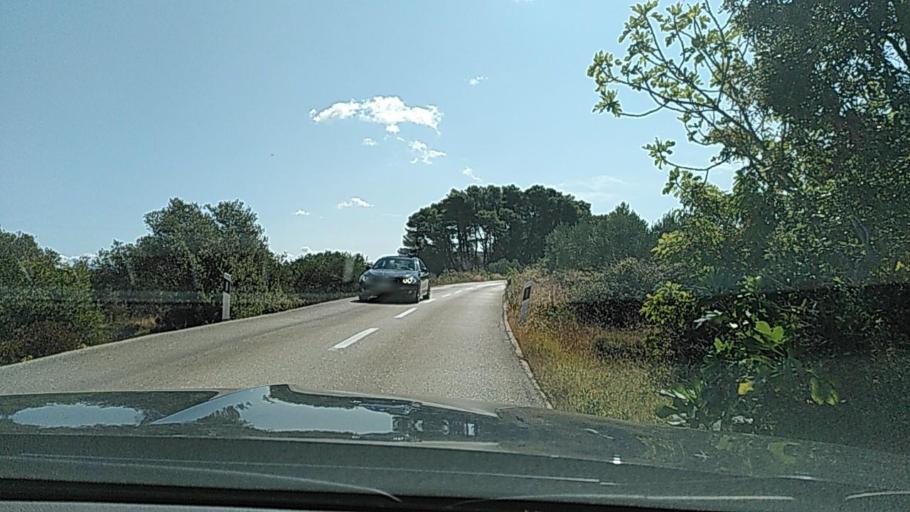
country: HR
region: Splitsko-Dalmatinska
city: Jelsa
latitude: 43.1488
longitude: 16.7974
